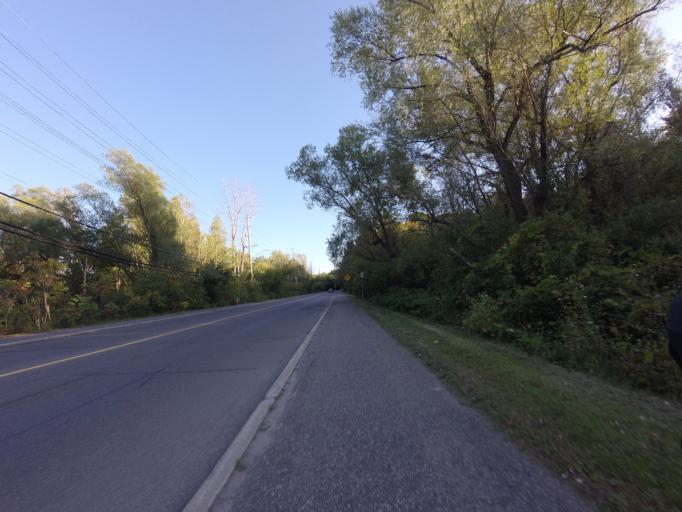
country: CA
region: Ontario
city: Ottawa
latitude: 45.3578
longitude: -75.6733
